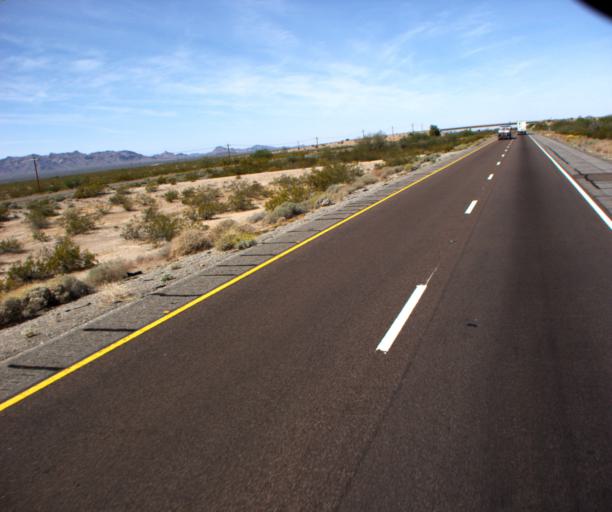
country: US
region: Arizona
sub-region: La Paz County
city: Salome
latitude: 33.5603
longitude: -113.2933
